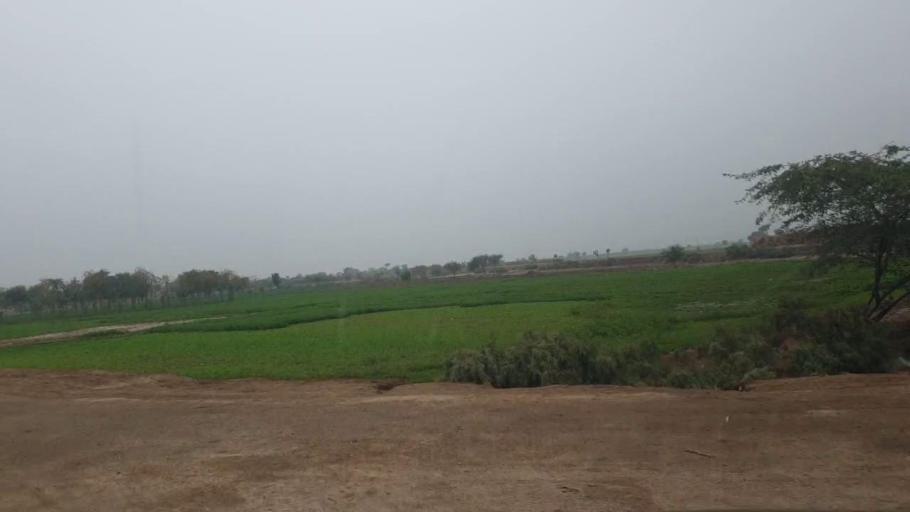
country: PK
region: Sindh
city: Tando Adam
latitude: 25.8289
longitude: 68.6816
